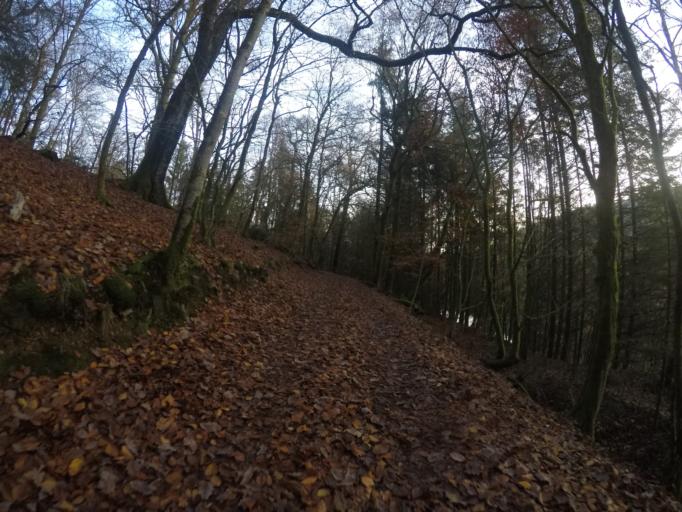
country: BE
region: Wallonia
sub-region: Province du Luxembourg
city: Habay-la-Vieille
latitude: 49.7411
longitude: 5.6716
